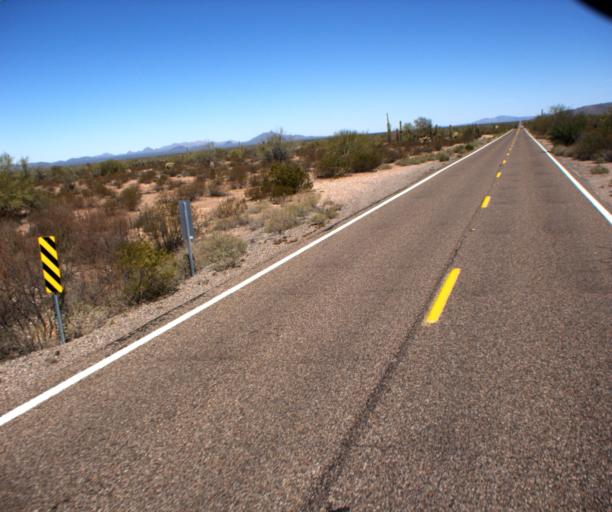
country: MX
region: Sonora
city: Sonoyta
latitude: 32.1167
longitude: -112.7692
